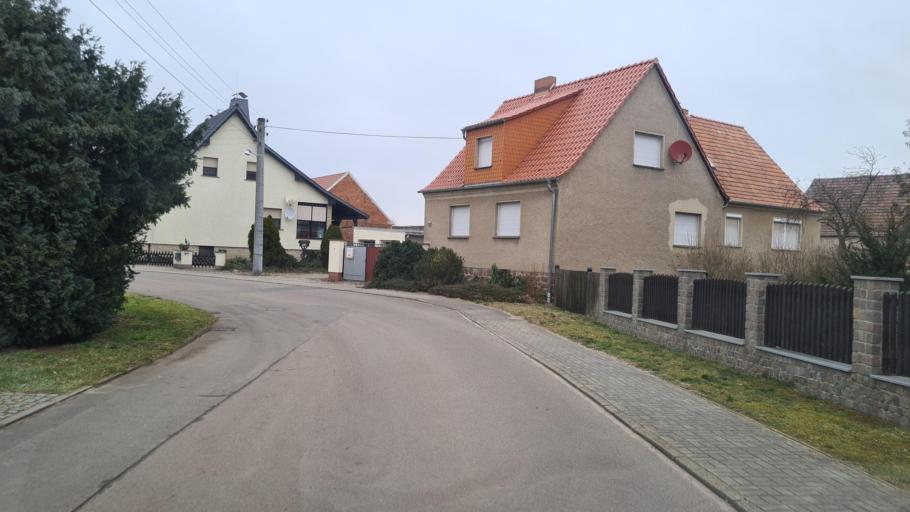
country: DE
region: Brandenburg
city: Herzberg
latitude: 51.6987
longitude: 13.1738
